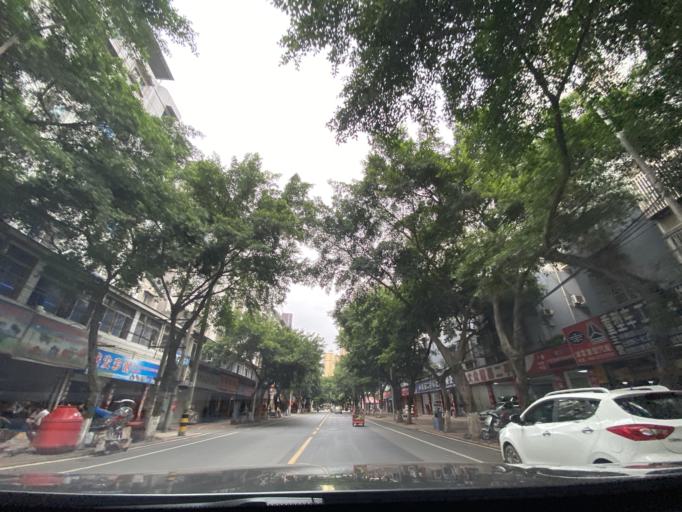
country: CN
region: Sichuan
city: Jiancheng
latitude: 30.3832
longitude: 104.5526
